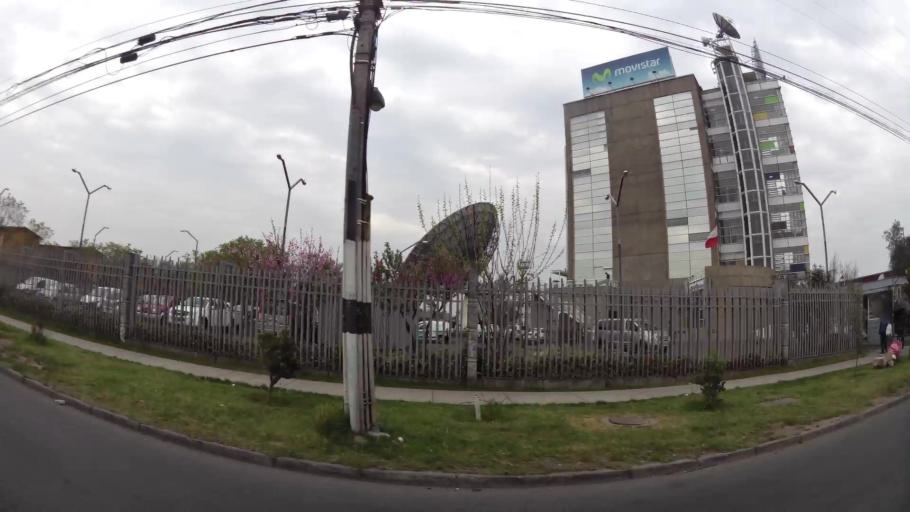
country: CL
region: Santiago Metropolitan
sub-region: Provincia de Santiago
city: Villa Presidente Frei, Nunoa, Santiago, Chile
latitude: -33.5052
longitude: -70.6036
